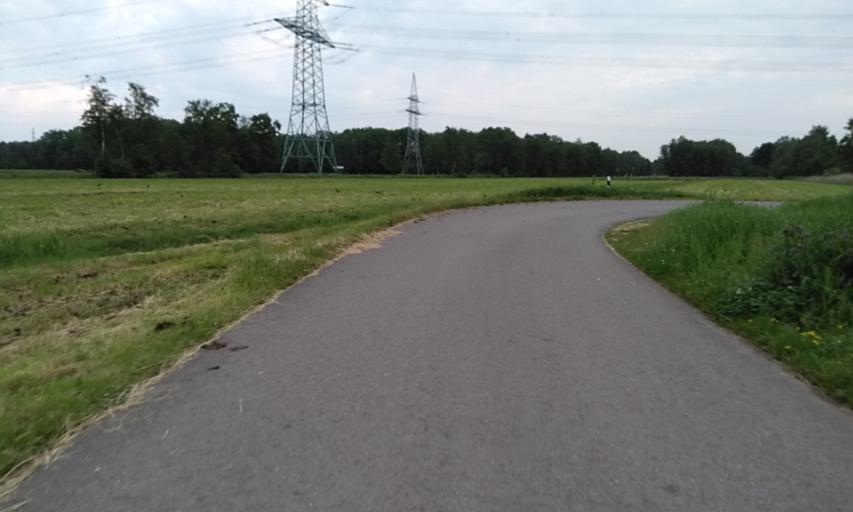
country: DE
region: Lower Saxony
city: Buxtehude
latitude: 53.4949
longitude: 9.6796
